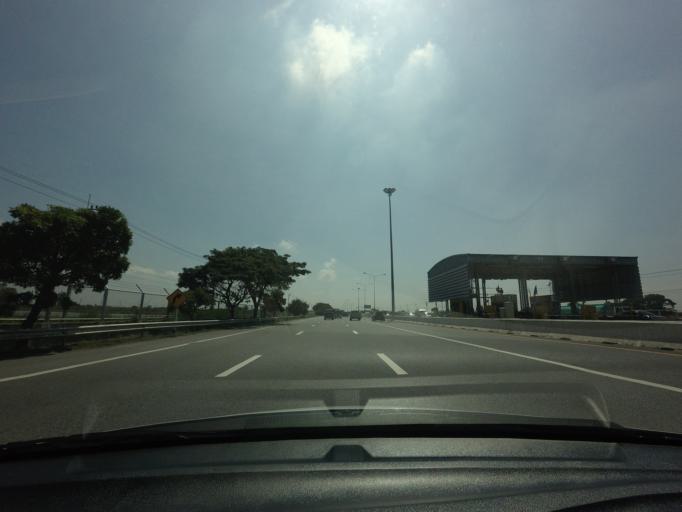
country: TH
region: Samut Prakan
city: Ban Khlong Bang Sao Thong
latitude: 13.6684
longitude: 100.8466
